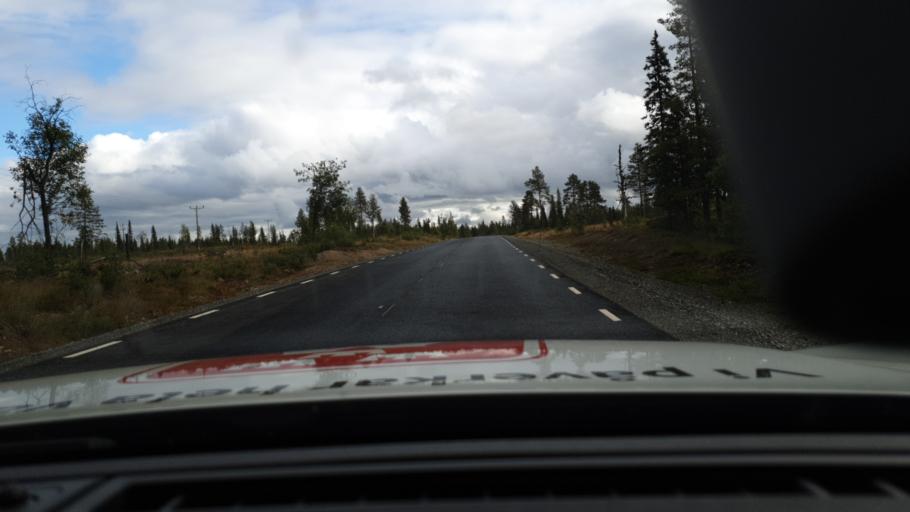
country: SE
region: Norrbotten
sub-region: Gallivare Kommun
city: Gaellivare
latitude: 66.8518
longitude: 21.0902
